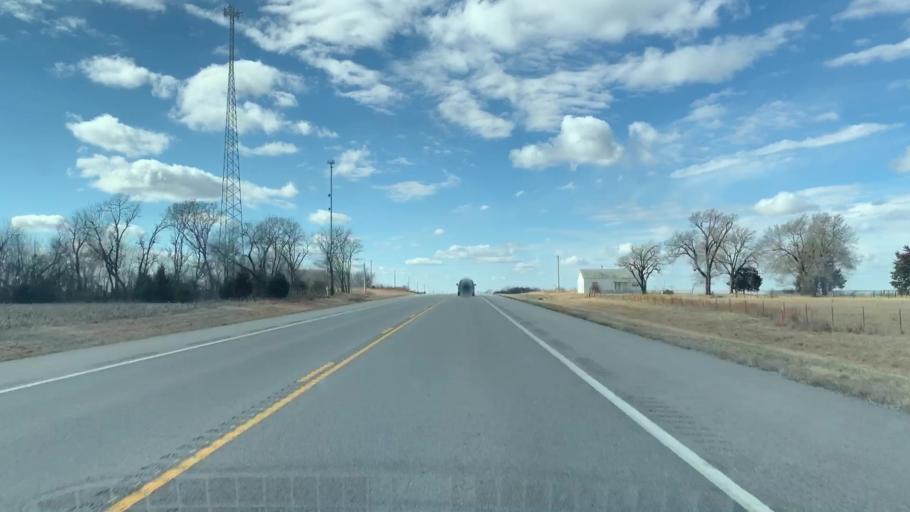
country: US
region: Kansas
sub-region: Labette County
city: Oswego
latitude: 37.3401
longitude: -95.0245
